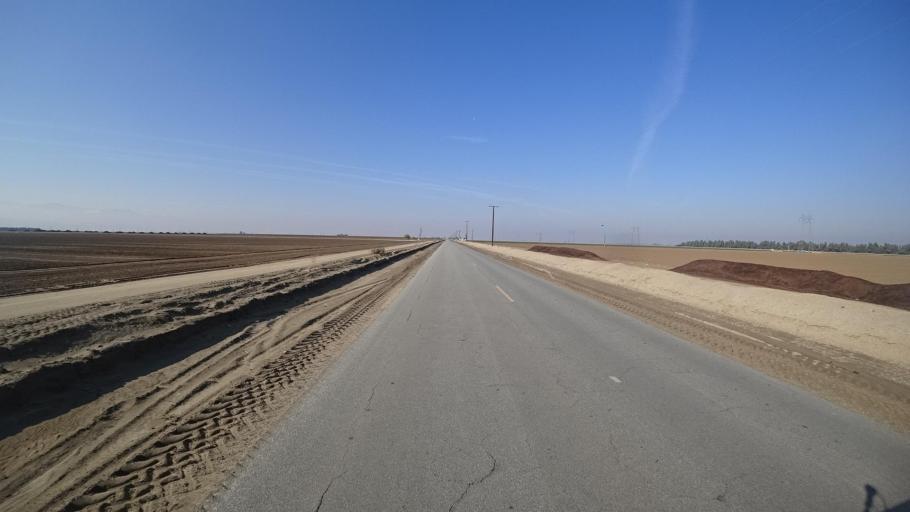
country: US
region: California
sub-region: Kern County
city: Weedpatch
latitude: 35.1221
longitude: -118.9555
